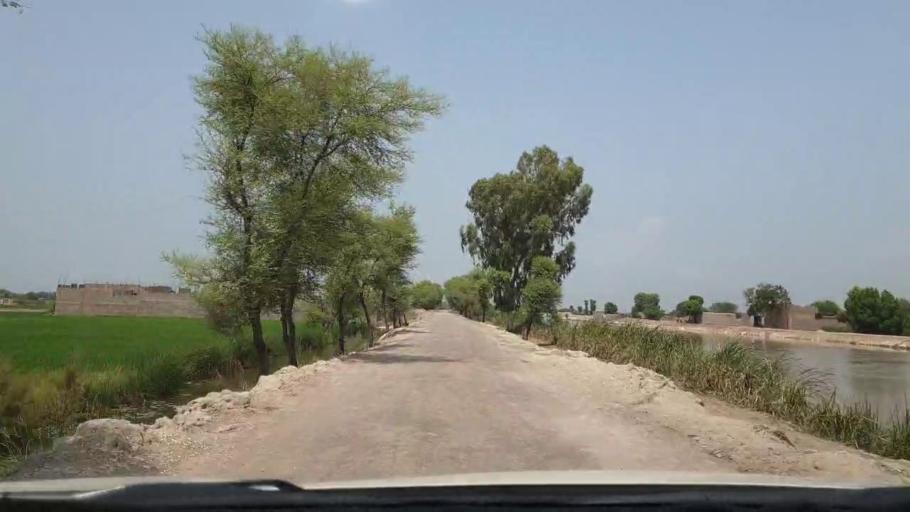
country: PK
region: Sindh
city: Dokri
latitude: 27.3357
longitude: 68.1102
